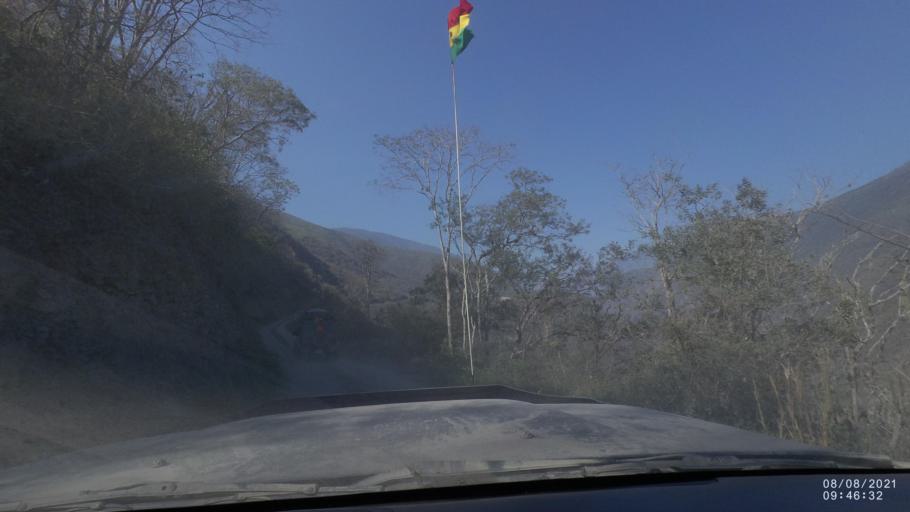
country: BO
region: La Paz
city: Quime
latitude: -16.6056
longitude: -66.7307
